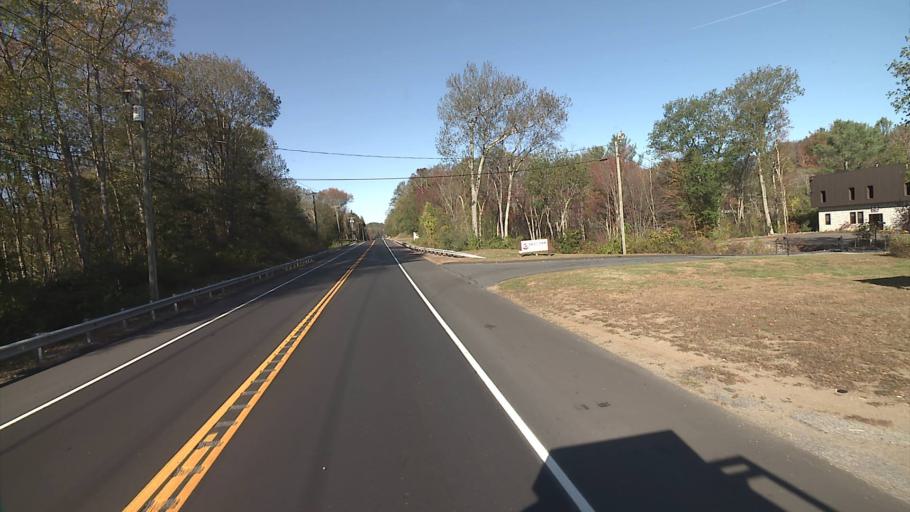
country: US
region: Connecticut
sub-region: Tolland County
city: South Coventry
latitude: 41.7255
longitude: -72.3096
